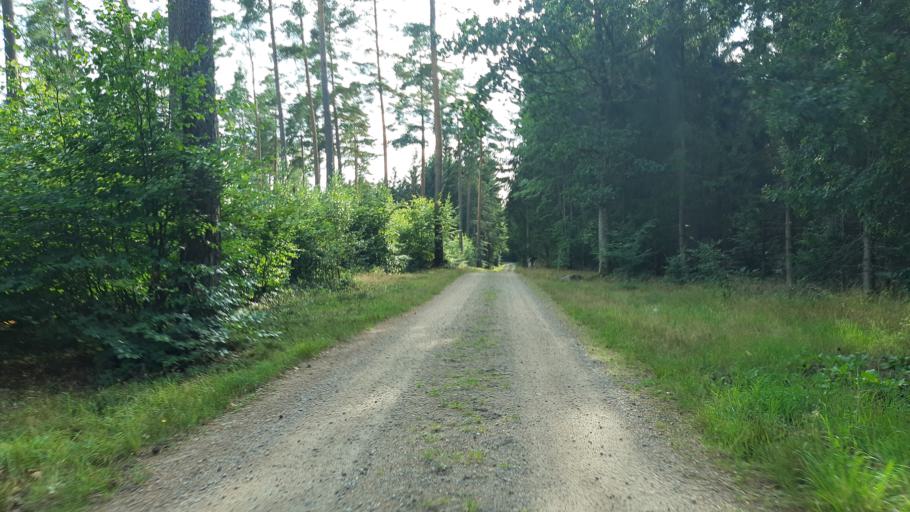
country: SE
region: Blekinge
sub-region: Ronneby Kommun
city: Kallinge
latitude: 56.2441
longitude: 15.4007
